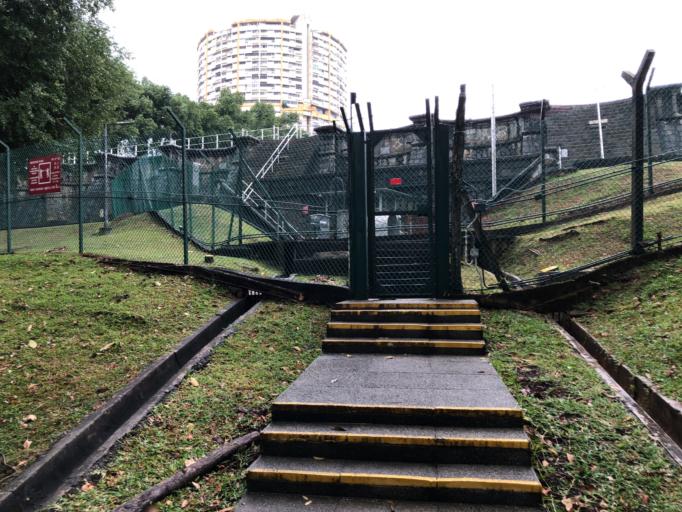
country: SG
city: Singapore
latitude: 1.2851
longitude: 103.8402
